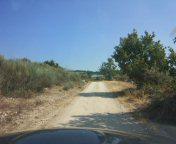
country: PT
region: Viseu
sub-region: Sernancelhe
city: Sernancelhe
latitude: 40.9369
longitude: -7.5065
